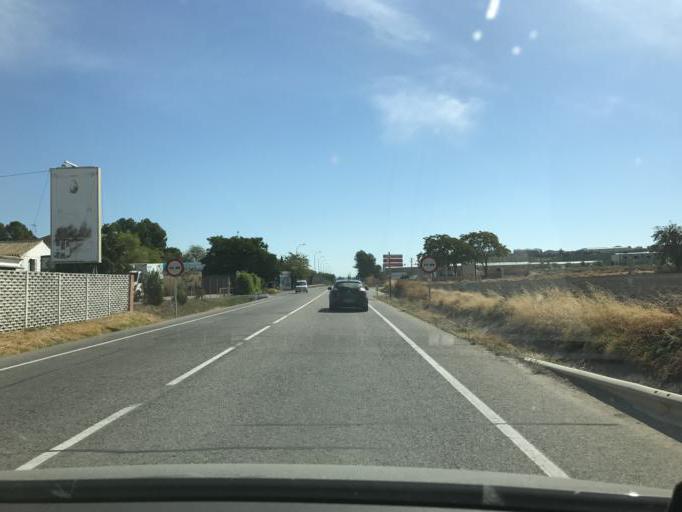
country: ES
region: Andalusia
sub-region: Province of Cordoba
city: Castro del Rio
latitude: 37.6843
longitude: -4.4780
